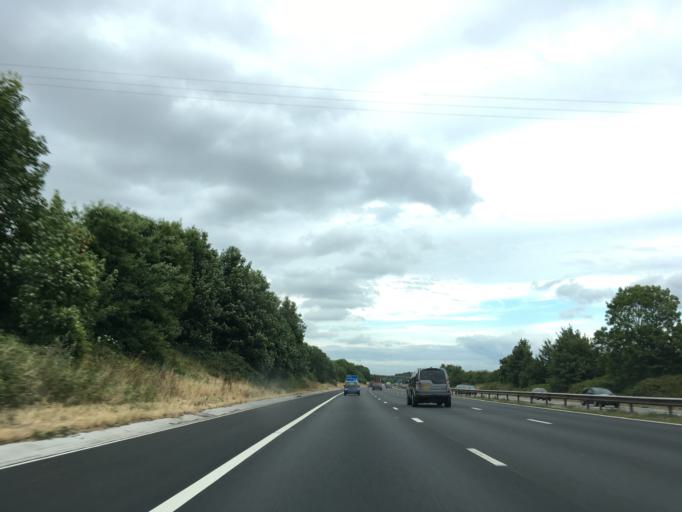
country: GB
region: England
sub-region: South Gloucestershire
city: Falfield
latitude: 51.6240
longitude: -2.4618
